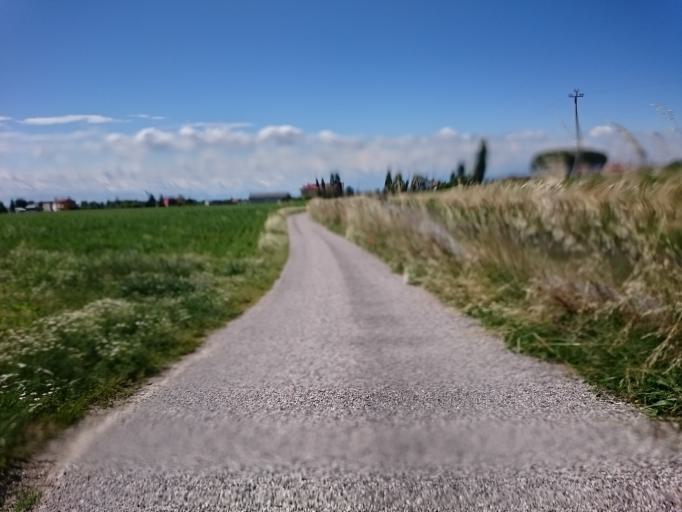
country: IT
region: Veneto
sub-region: Provincia di Padova
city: Codevigo
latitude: 45.2565
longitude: 12.0981
